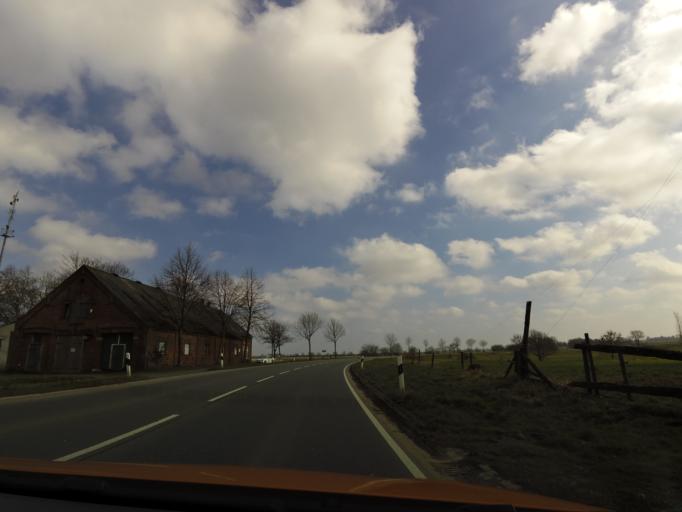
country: DE
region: Lower Saxony
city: Varel
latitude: 53.3937
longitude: 8.1748
